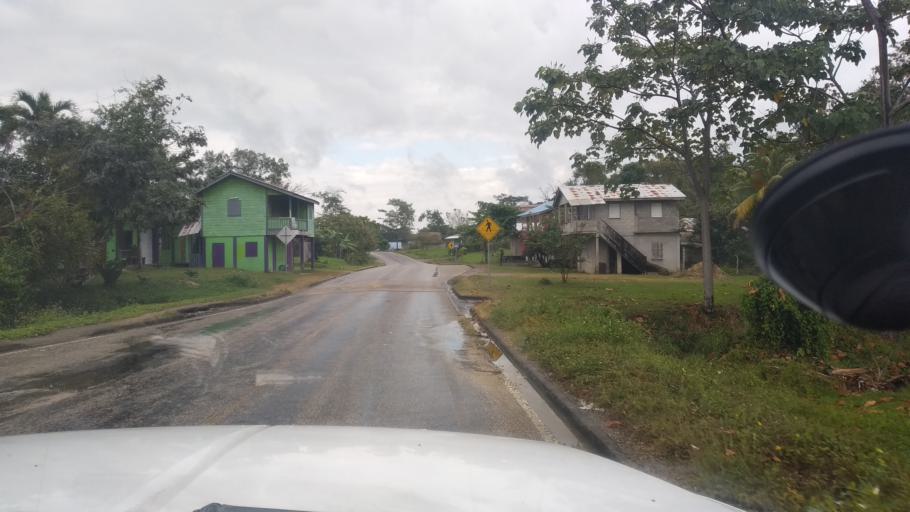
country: GT
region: Peten
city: San Luis
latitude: 16.2073
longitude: -89.1391
